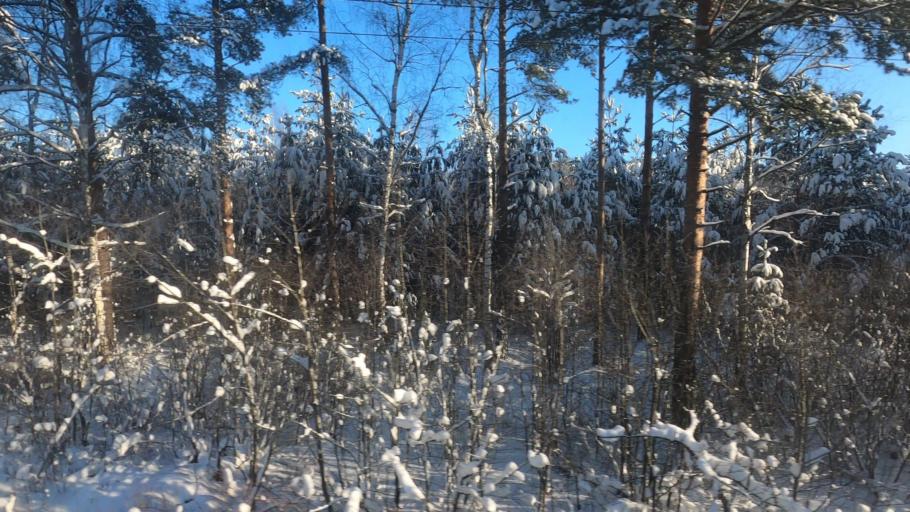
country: RU
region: Moskovskaya
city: Zhukovka
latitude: 56.4608
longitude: 37.5261
